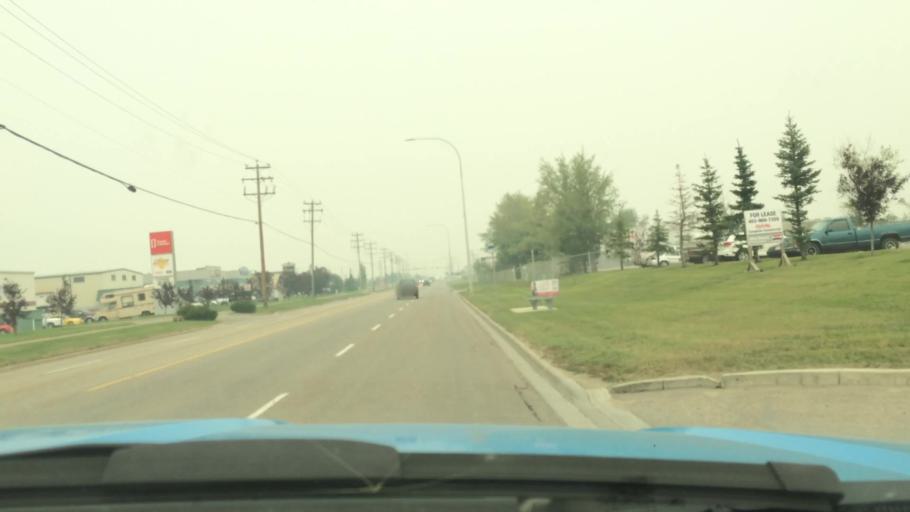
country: CA
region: Alberta
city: Airdrie
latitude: 51.2962
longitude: -113.9899
